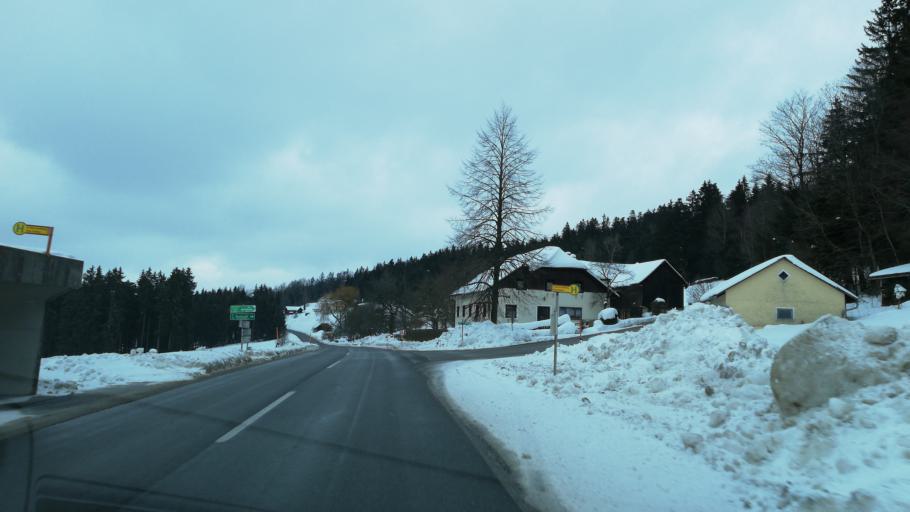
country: AT
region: Upper Austria
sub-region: Politischer Bezirk Urfahr-Umgebung
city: Herzogsdorf
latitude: 48.4744
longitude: 14.1397
